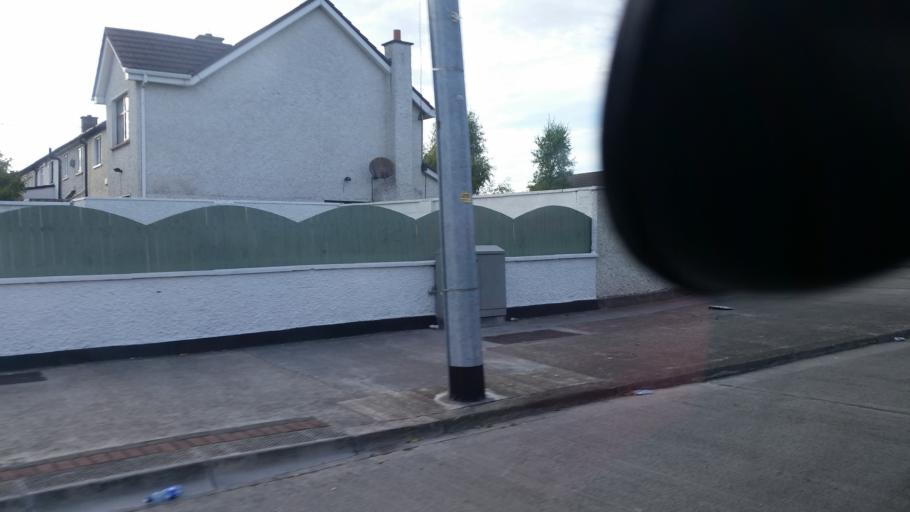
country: IE
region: Leinster
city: Beaumont
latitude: 53.3947
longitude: -6.2325
